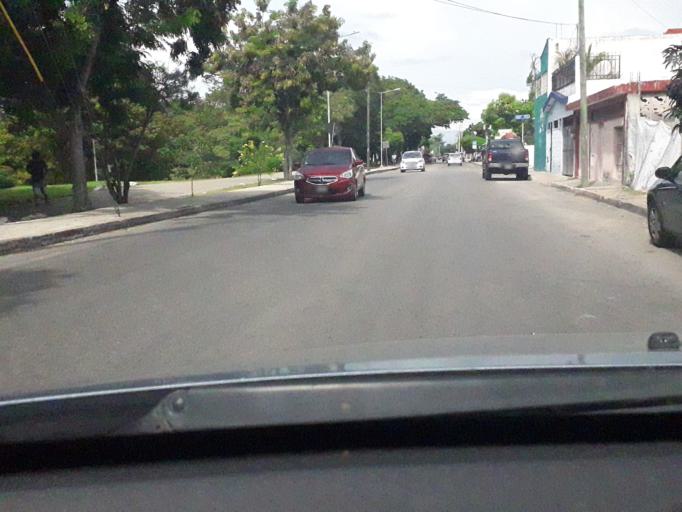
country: MX
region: Yucatan
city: Merida
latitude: 20.9747
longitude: -89.6558
